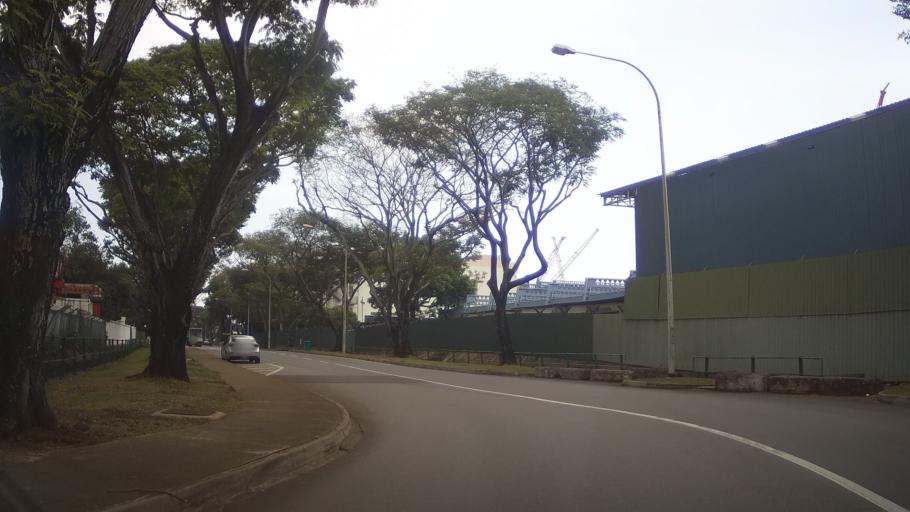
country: SG
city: Singapore
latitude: 1.3031
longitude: 103.6764
